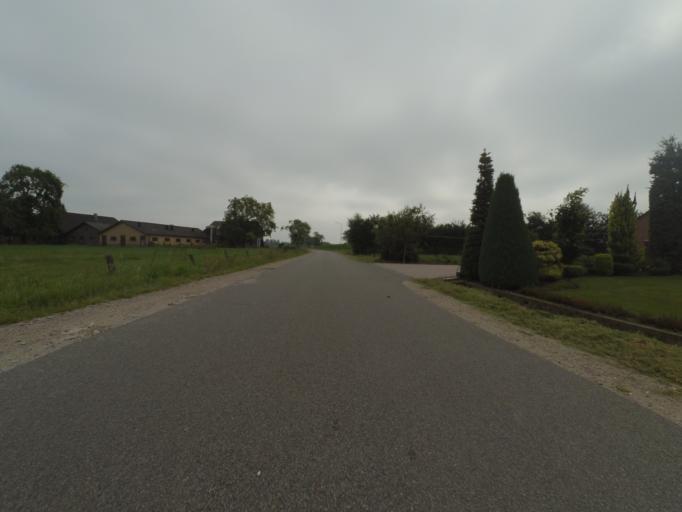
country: NL
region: Gelderland
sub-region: Gemeente Barneveld
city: Kootwijkerbroek
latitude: 52.1382
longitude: 5.6422
